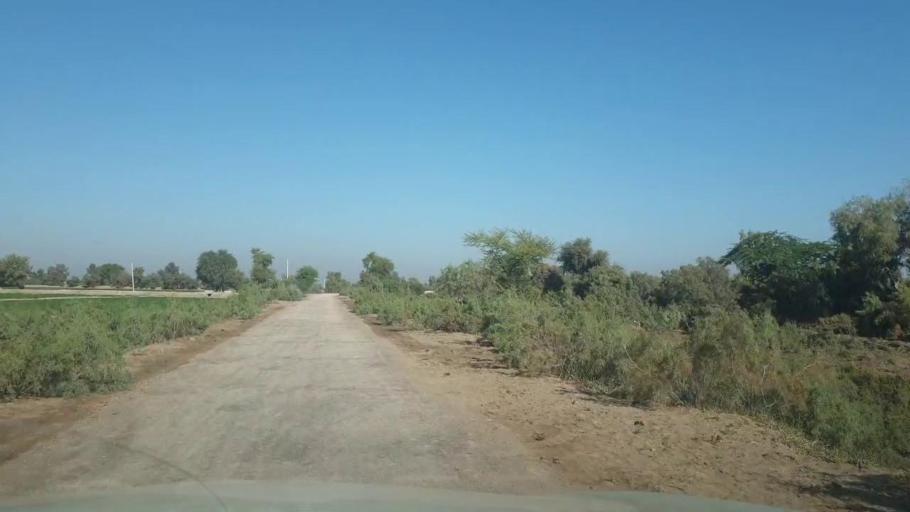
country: PK
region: Sindh
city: Bhan
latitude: 26.5385
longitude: 67.6583
